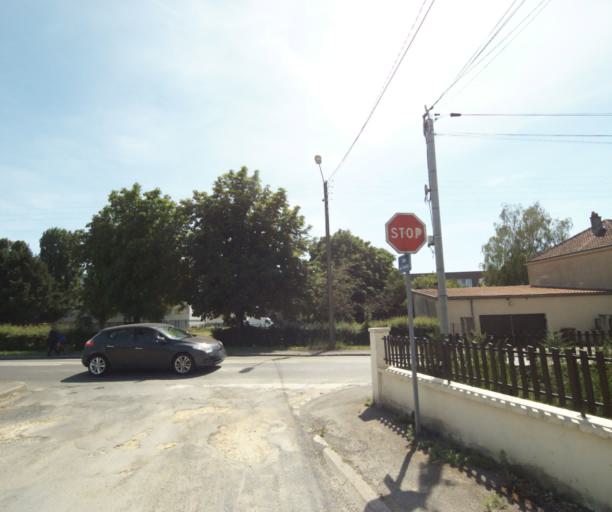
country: FR
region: Champagne-Ardenne
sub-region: Departement des Ardennes
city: Prix-les-Mezieres
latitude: 49.7663
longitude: 4.6896
